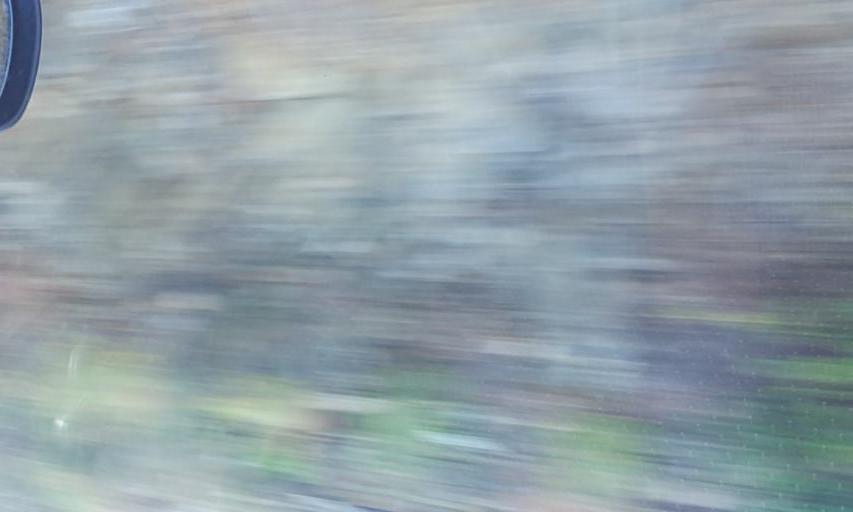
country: PT
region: Viseu
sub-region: Sao Joao da Pesqueira
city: Sao Joao da Pesqueira
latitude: 41.2361
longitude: -7.4303
